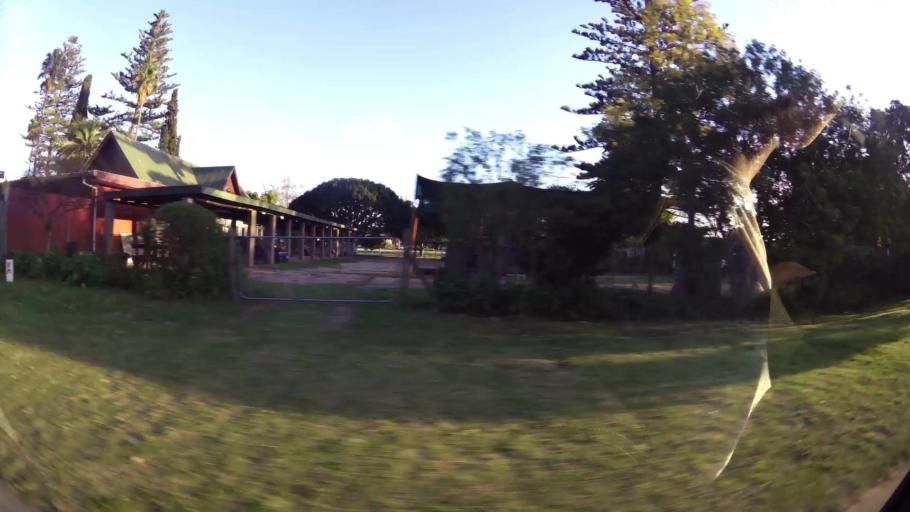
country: ZA
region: Western Cape
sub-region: Eden District Municipality
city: Knysna
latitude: -34.0134
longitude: 22.8023
